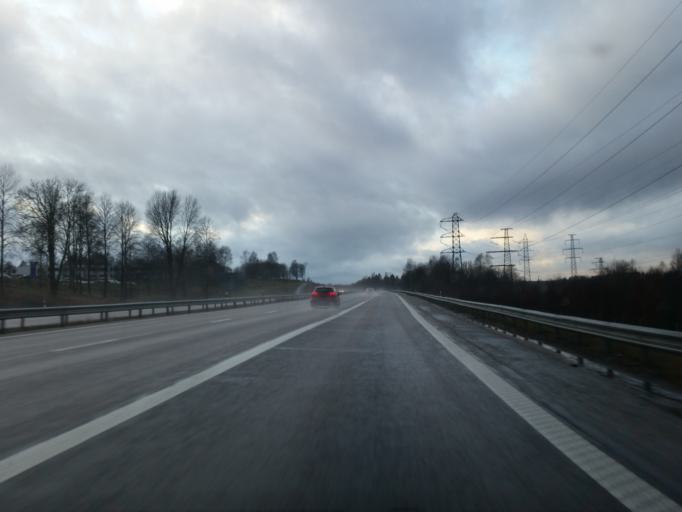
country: SE
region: Vaestra Goetaland
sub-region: Boras Kommun
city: Sjomarken
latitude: 57.7112
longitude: 12.8634
